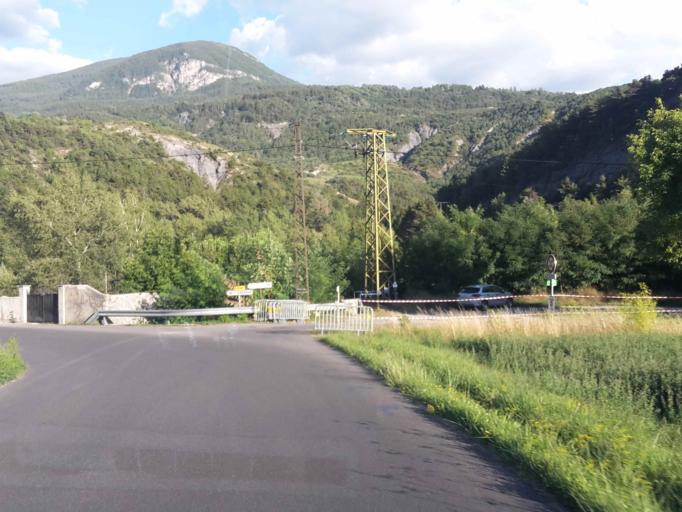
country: FR
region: Provence-Alpes-Cote d'Azur
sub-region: Departement des Hautes-Alpes
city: Embrun
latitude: 44.5611
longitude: 6.5098
